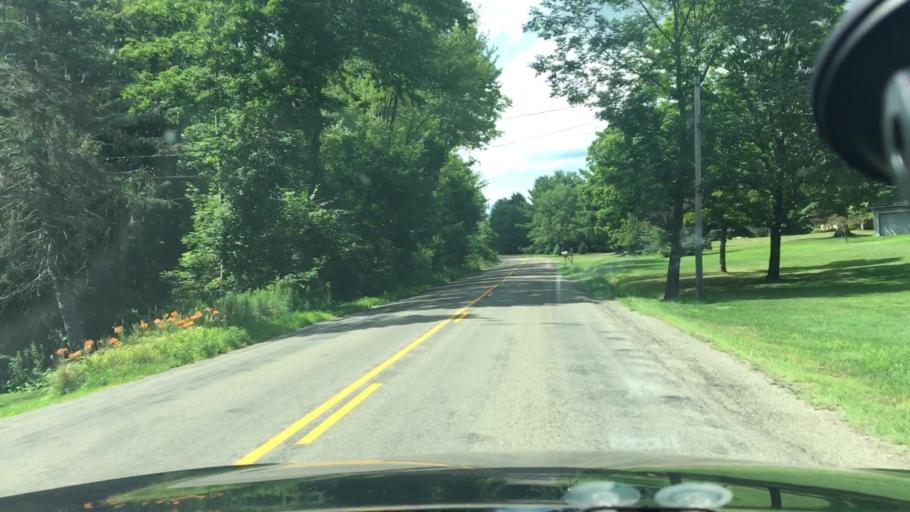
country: US
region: New York
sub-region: Chautauqua County
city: Lakewood
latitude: 42.1019
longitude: -79.3792
